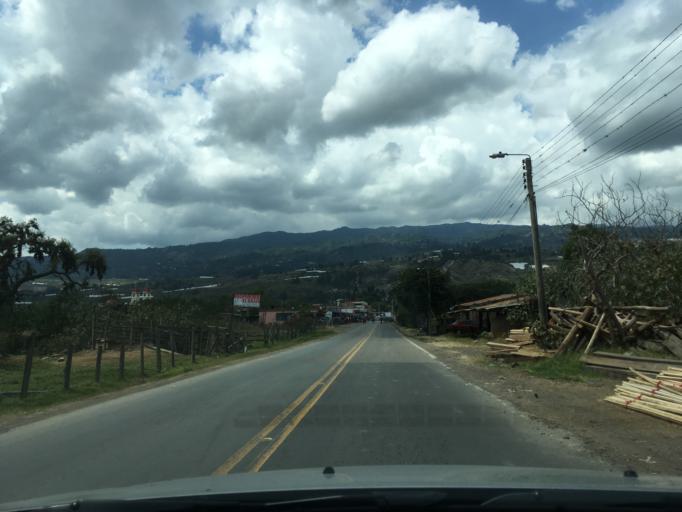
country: CO
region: Boyaca
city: Sutamarchan
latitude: 5.6199
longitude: -73.6158
